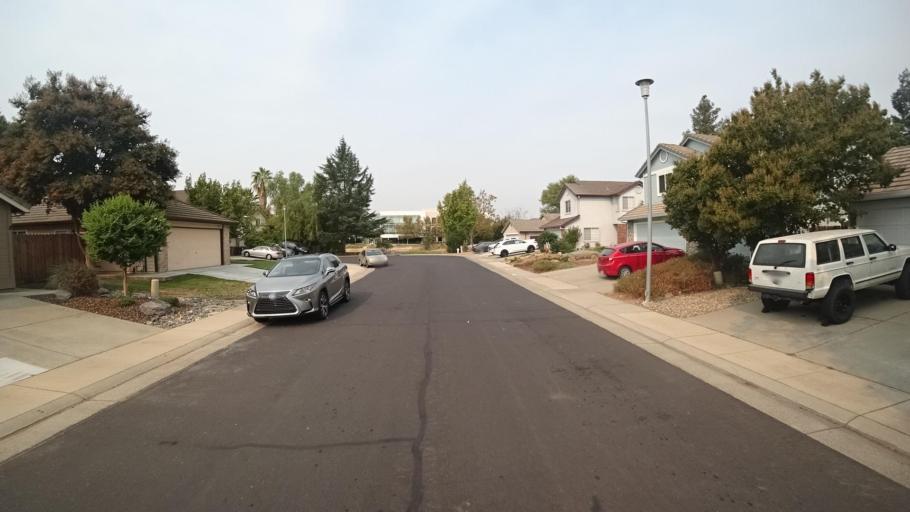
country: US
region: California
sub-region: Sacramento County
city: Laguna
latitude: 38.4190
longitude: -121.3979
